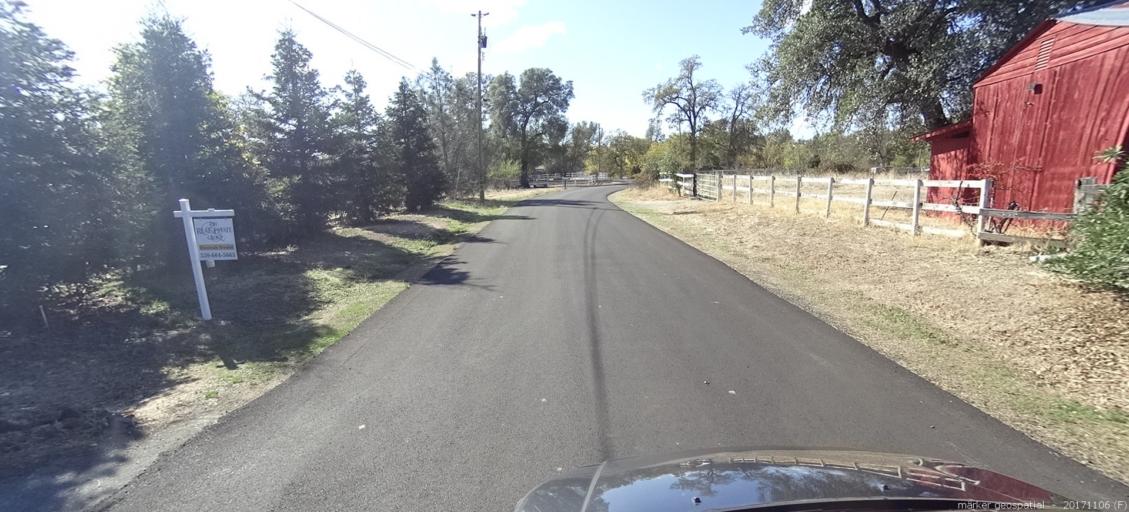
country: US
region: California
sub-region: Shasta County
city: Palo Cedro
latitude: 40.5889
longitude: -122.2227
